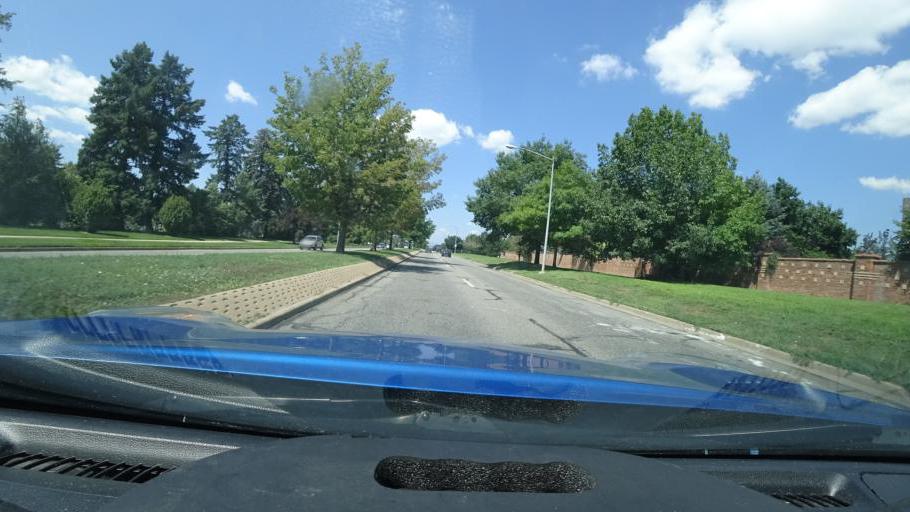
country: US
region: Colorado
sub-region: Arapahoe County
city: Glendale
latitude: 39.7113
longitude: -104.8993
